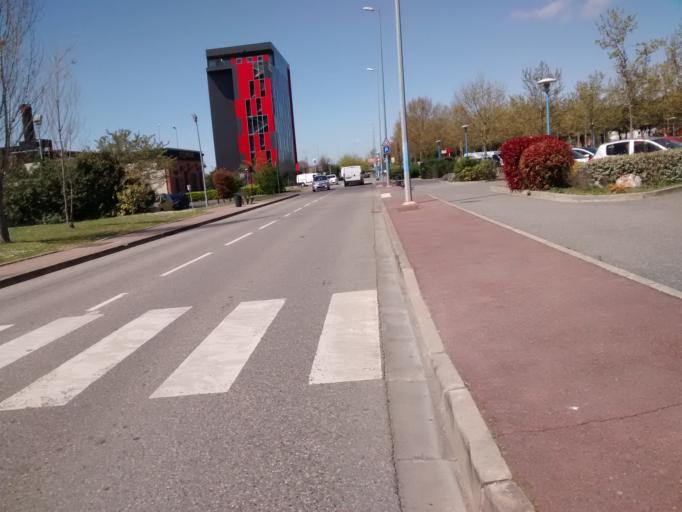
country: FR
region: Midi-Pyrenees
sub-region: Departement de la Haute-Garonne
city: Saint-Orens-de-Gameville
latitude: 43.5409
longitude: 1.5140
